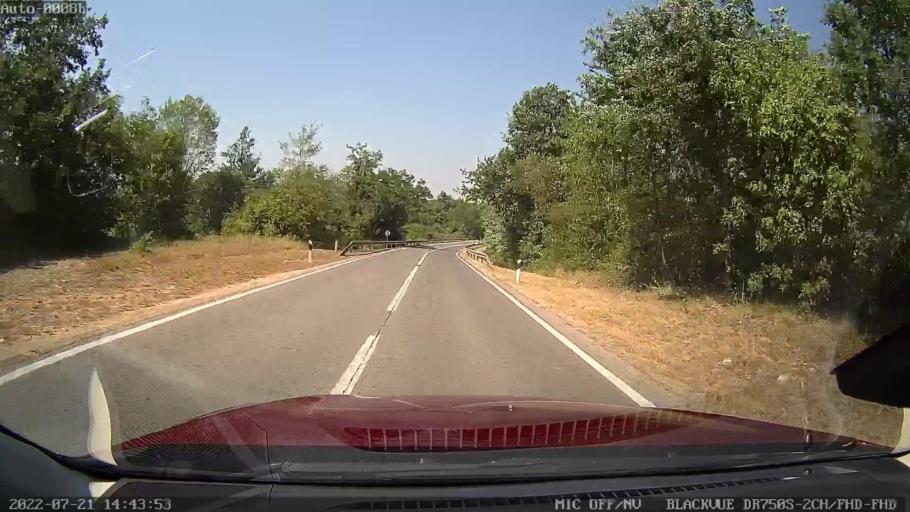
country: HR
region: Istarska
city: Pazin
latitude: 45.1123
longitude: 13.8828
